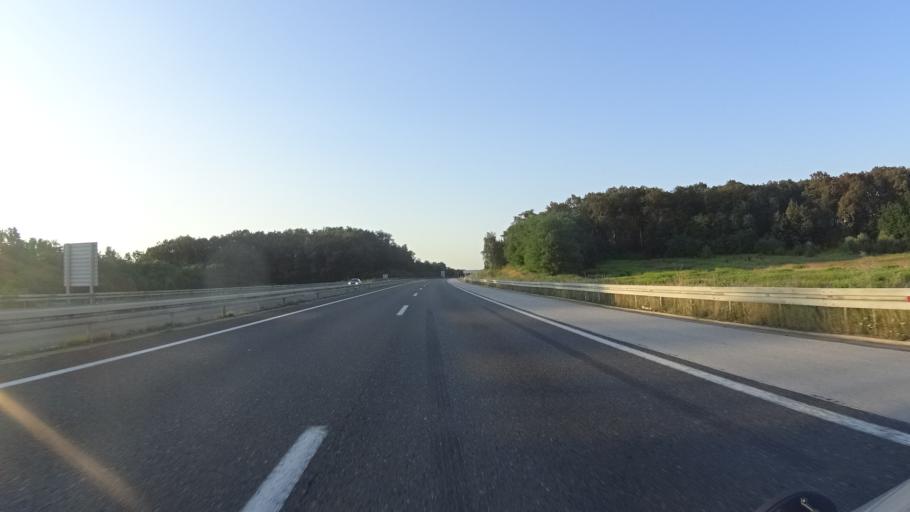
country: HR
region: Grad Zagreb
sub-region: Sesvete
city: Sesvete
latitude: 45.8325
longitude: 16.1374
